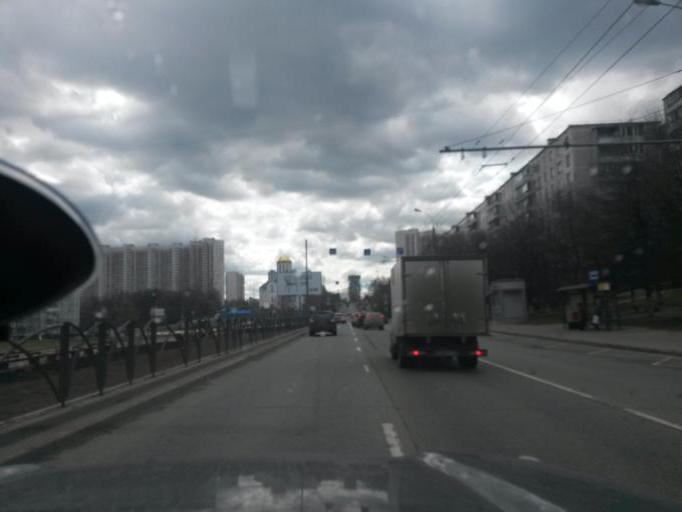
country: RU
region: Moscow
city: Yasenevo
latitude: 55.6182
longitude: 37.5412
